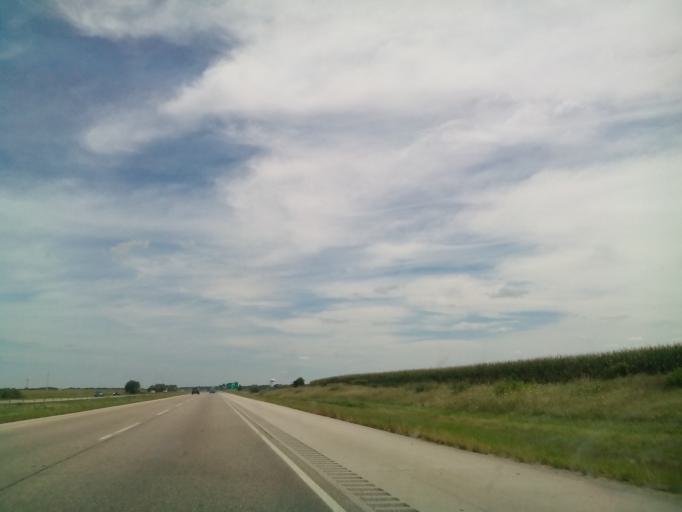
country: US
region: Illinois
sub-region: DeKalb County
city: DeKalb
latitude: 41.9001
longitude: -88.8046
